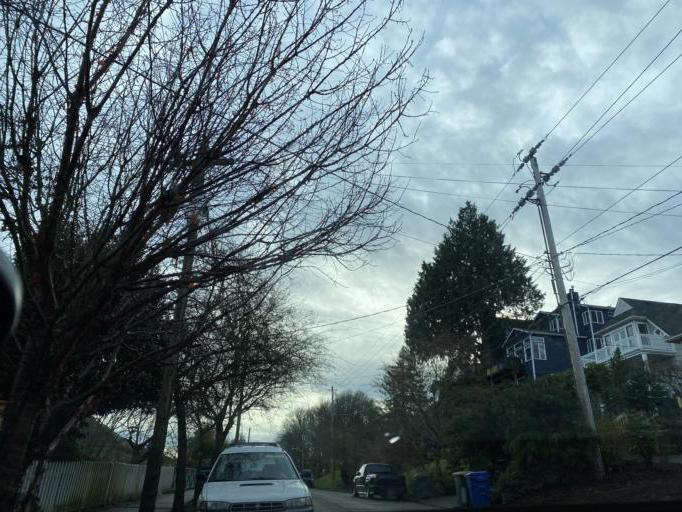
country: US
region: Washington
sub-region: King County
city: Seattle
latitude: 47.6464
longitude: -122.3859
